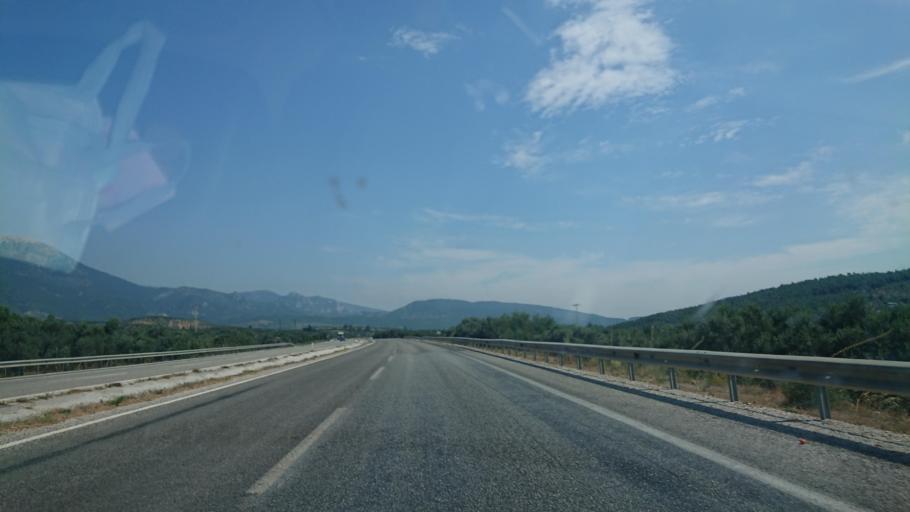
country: TR
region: Izmir
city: Dagkizilca
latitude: 38.2997
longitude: 27.4092
